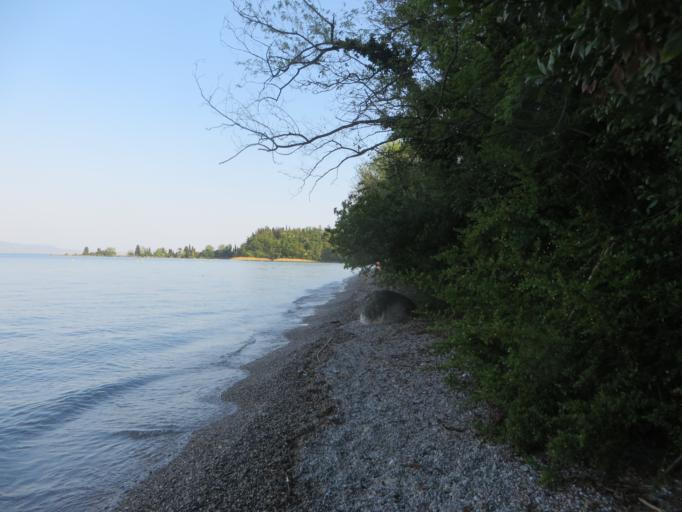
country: IT
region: Lombardy
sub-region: Provincia di Brescia
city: San Felice del Benaco
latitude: 45.5932
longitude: 10.5677
